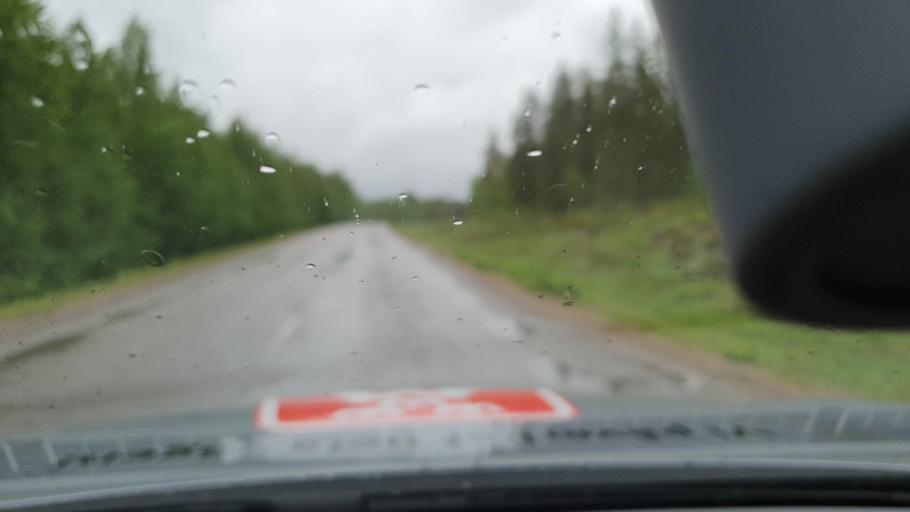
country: SE
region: Norrbotten
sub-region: Overkalix Kommun
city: OEverkalix
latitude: 66.4427
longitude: 23.0393
